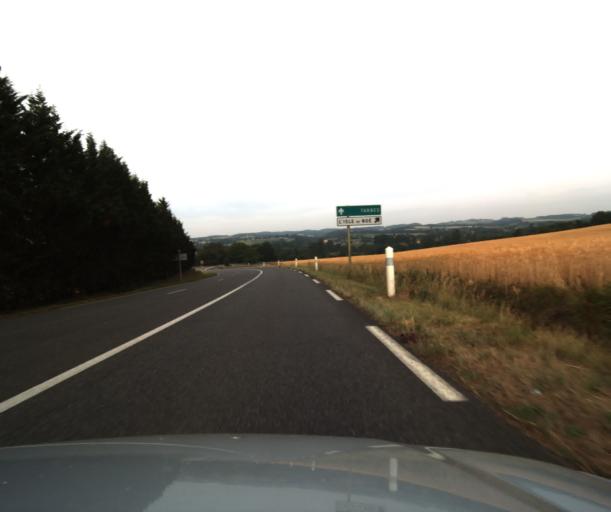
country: FR
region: Midi-Pyrenees
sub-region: Departement du Gers
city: Mirande
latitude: 43.5339
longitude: 0.4225
